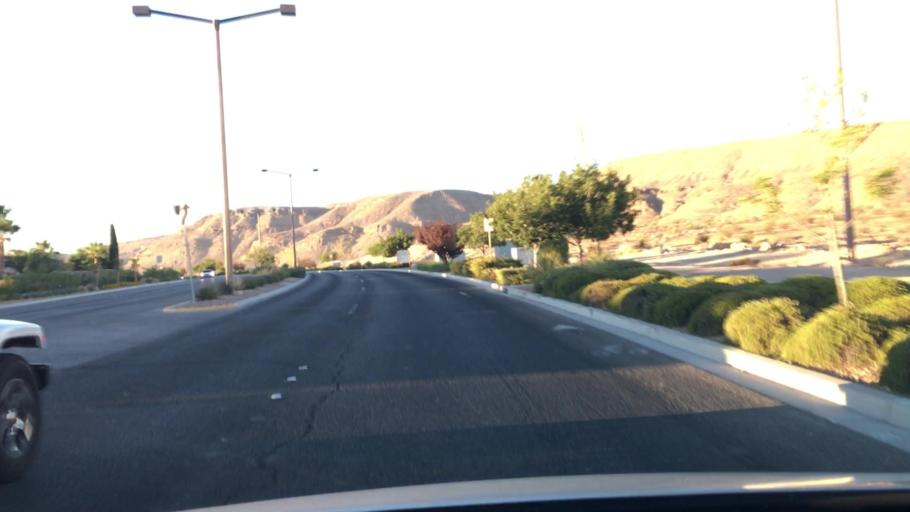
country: US
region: Nevada
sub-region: Clark County
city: Summerlin South
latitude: 36.0982
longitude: -115.3254
